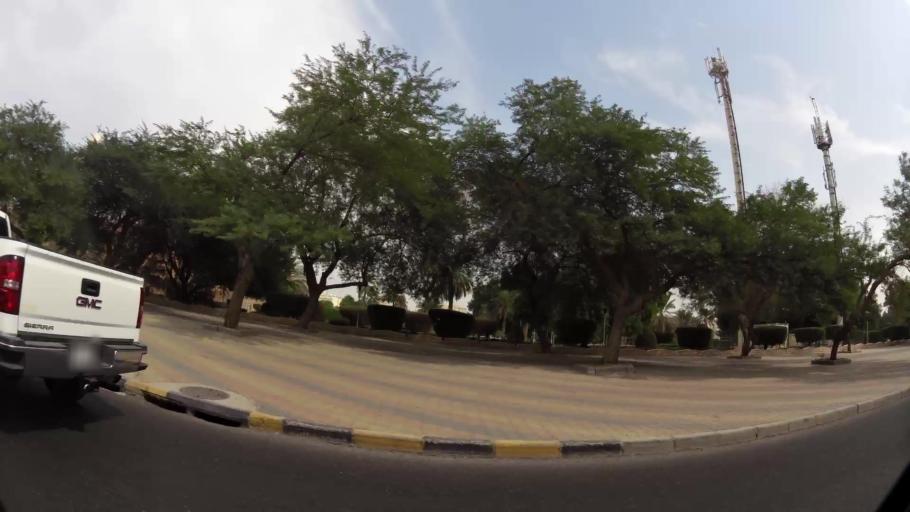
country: KW
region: Al Asimah
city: Ash Shamiyah
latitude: 29.3314
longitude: 47.9891
